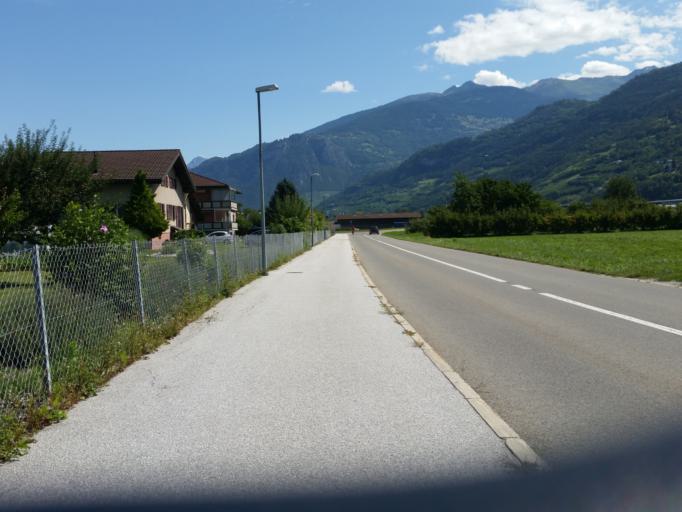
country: CH
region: Valais
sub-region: Sion District
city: Sitten
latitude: 46.2240
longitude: 7.3433
